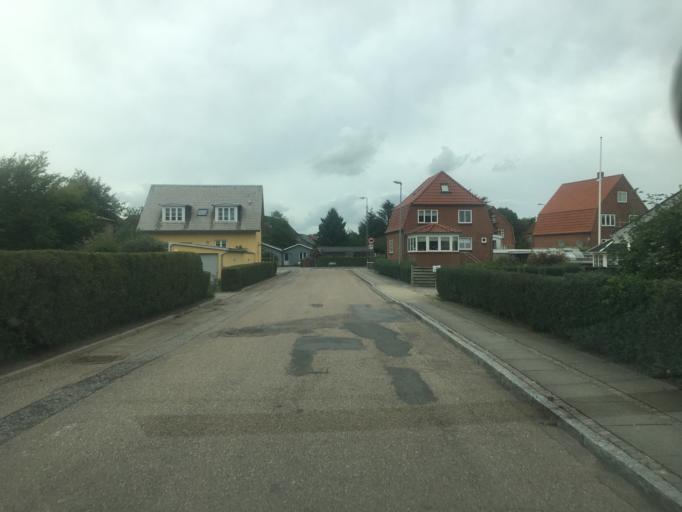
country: DK
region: South Denmark
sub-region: Tonder Kommune
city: Tonder
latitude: 54.9307
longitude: 8.8568
